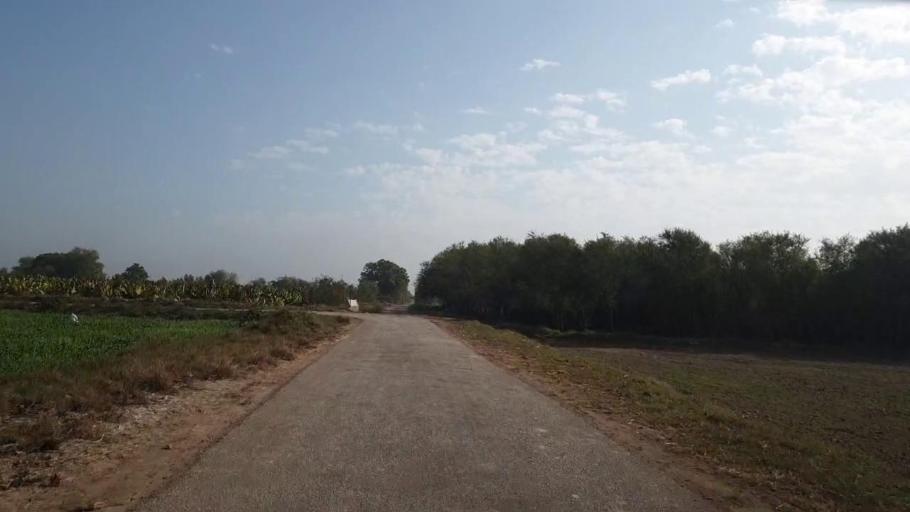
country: PK
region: Sindh
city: Matiari
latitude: 25.5998
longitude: 68.4966
